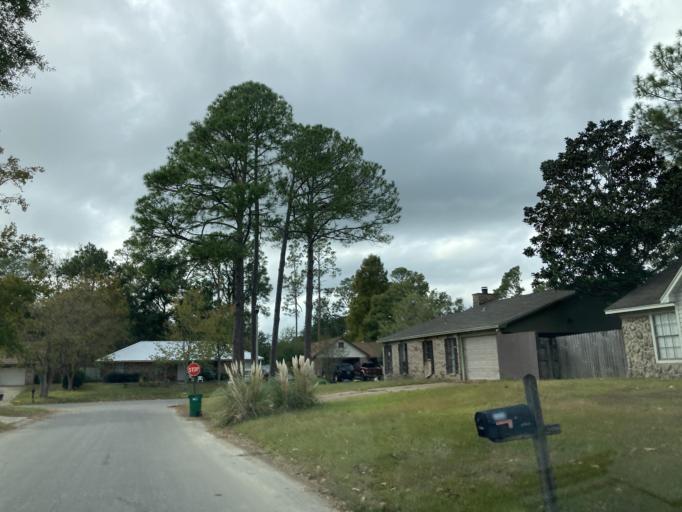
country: US
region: Mississippi
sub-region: Jackson County
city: Gulf Hills
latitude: 30.4373
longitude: -88.8191
